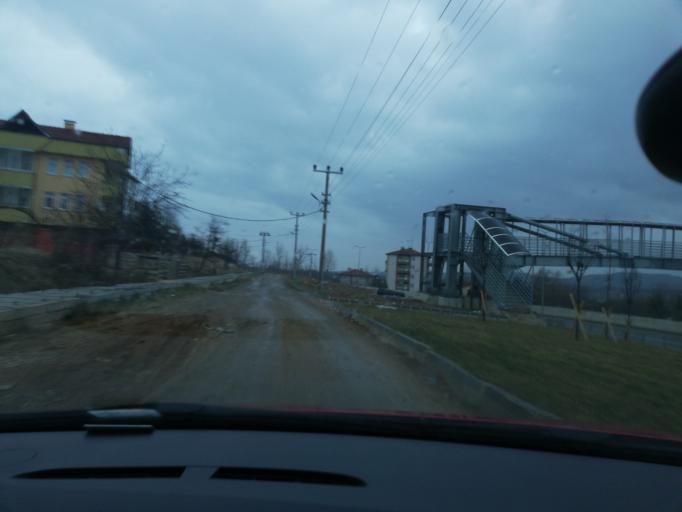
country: TR
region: Kastamonu
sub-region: Cide
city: Kastamonu
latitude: 41.4185
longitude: 33.7998
